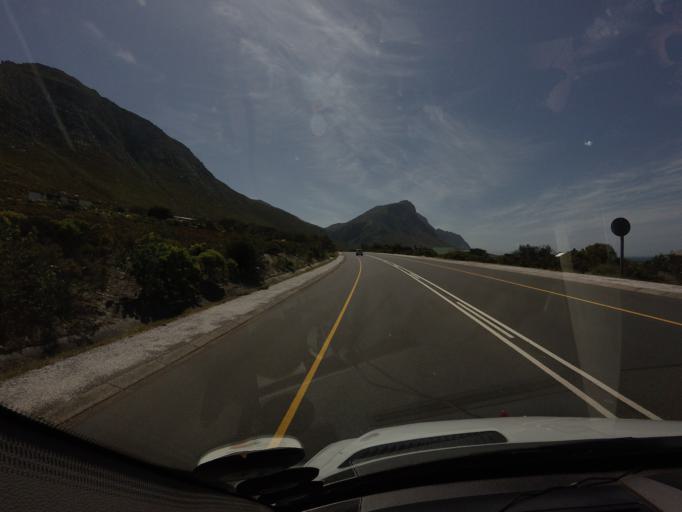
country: ZA
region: Western Cape
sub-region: Overberg District Municipality
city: Grabouw
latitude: -34.3526
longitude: 18.9129
